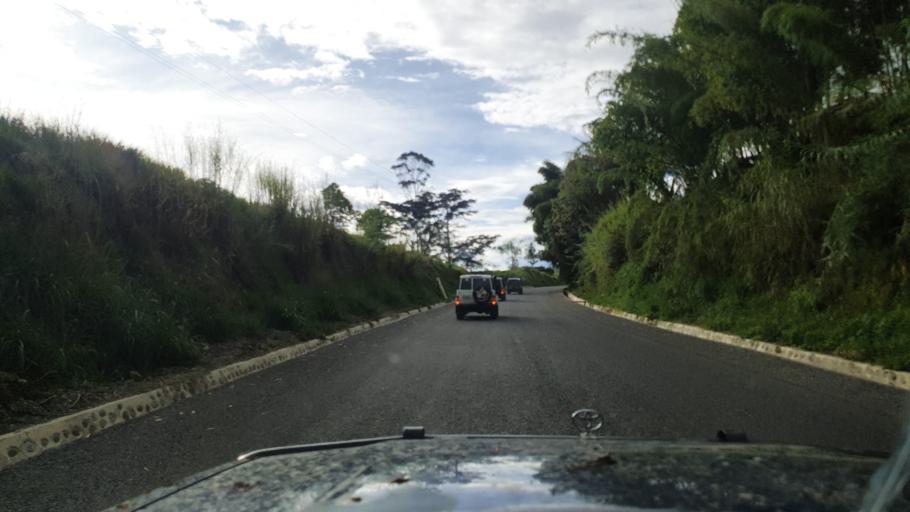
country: PG
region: Jiwaka
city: Minj
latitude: -5.9099
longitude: 144.7550
